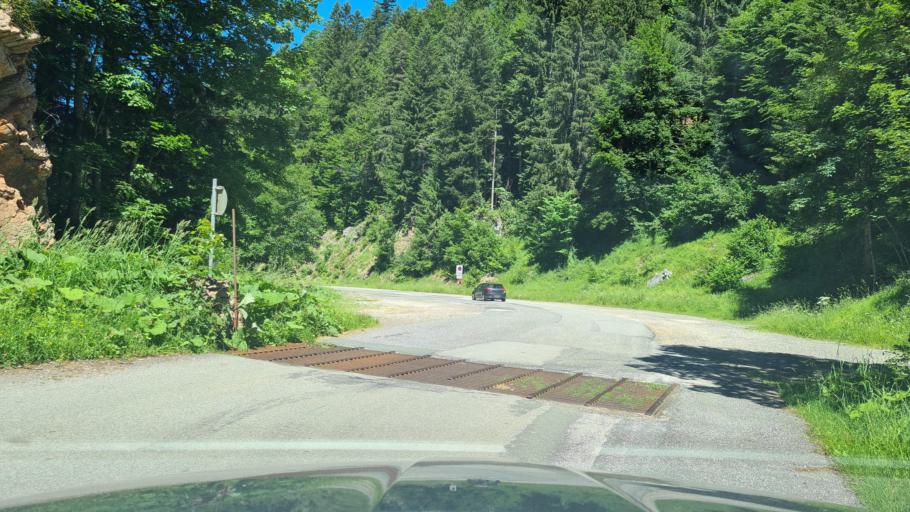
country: AT
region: Salzburg
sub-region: Politischer Bezirk Zell am See
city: Unken
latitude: 47.6527
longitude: 12.6796
